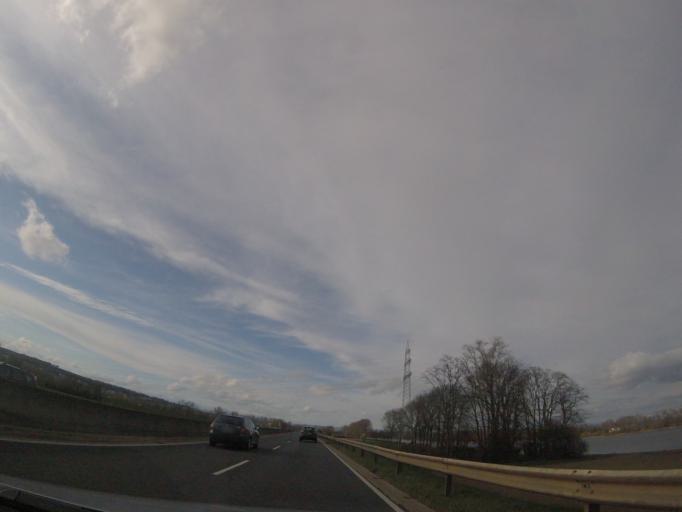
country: DE
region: Hesse
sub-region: Regierungsbezirk Darmstadt
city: Ginsheim-Gustavsburg
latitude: 49.9519
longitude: 8.3366
